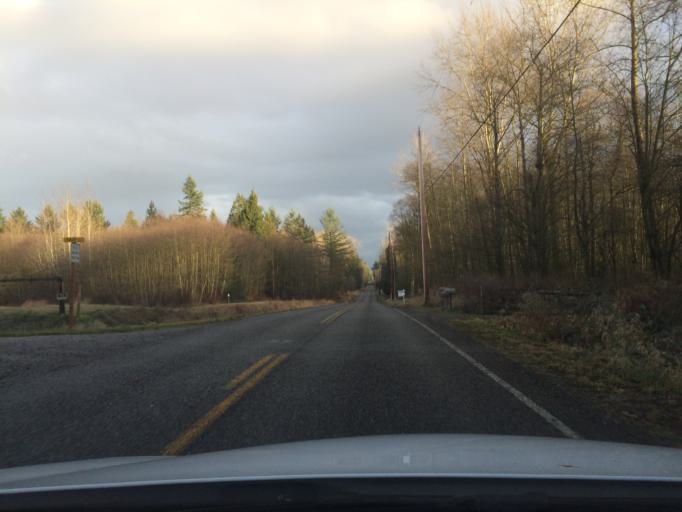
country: CA
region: British Columbia
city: Langley
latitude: 48.9936
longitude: -122.6066
